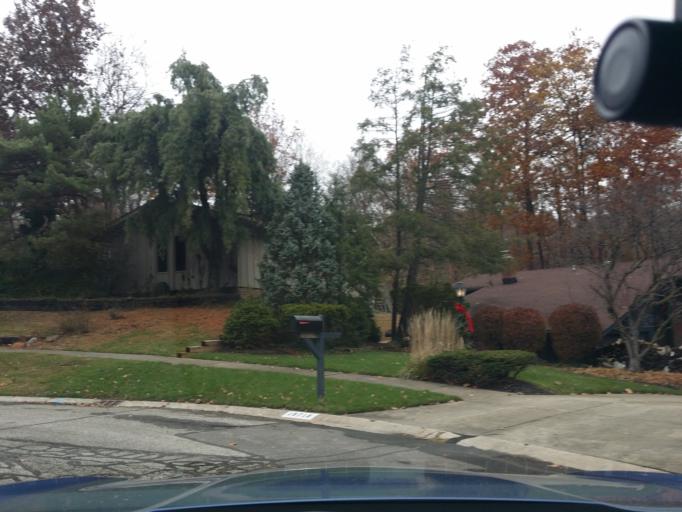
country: US
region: Ohio
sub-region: Cuyahoga County
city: Strongsville
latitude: 41.3322
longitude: -81.8434
